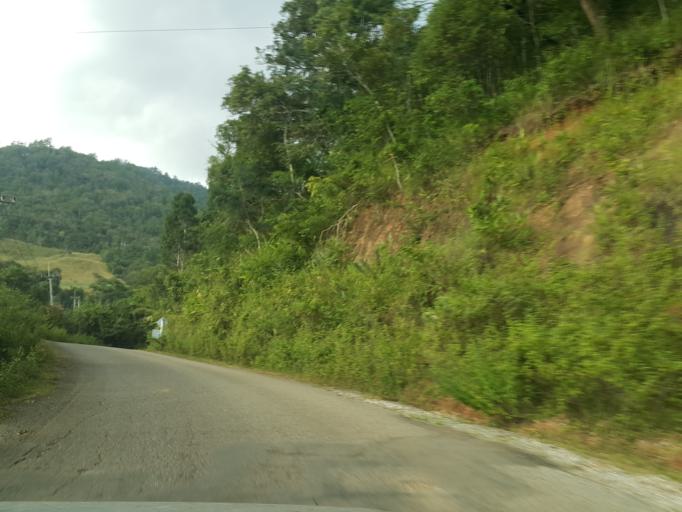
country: TH
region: Mae Hong Son
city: Khun Yuam
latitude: 18.7586
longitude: 98.1877
